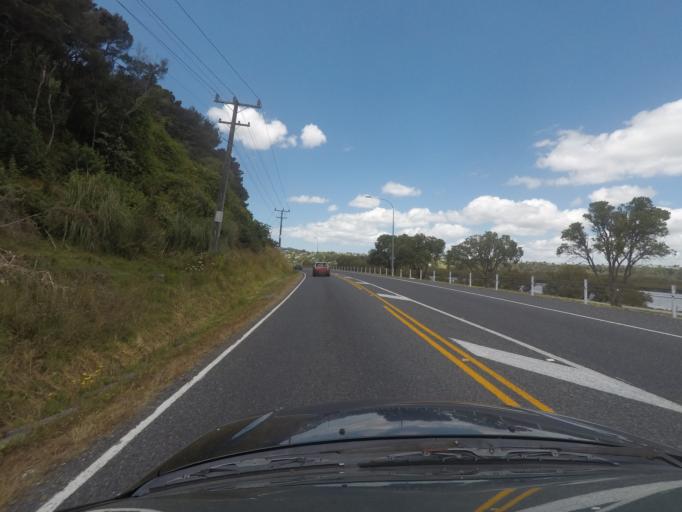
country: NZ
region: Northland
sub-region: Whangarei
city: Whangarei
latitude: -35.7362
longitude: 174.3522
